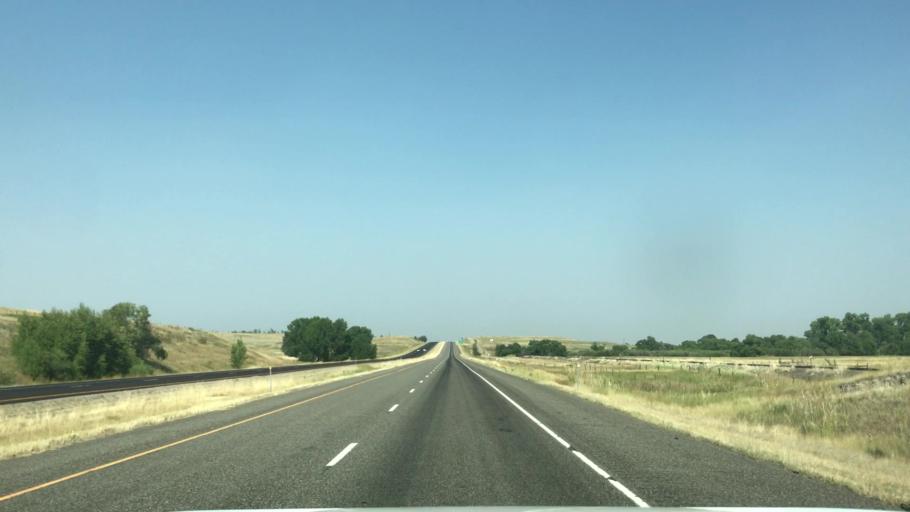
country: US
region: Montana
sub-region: Cascade County
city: Sun Prairie
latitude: 47.2410
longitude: -111.7295
